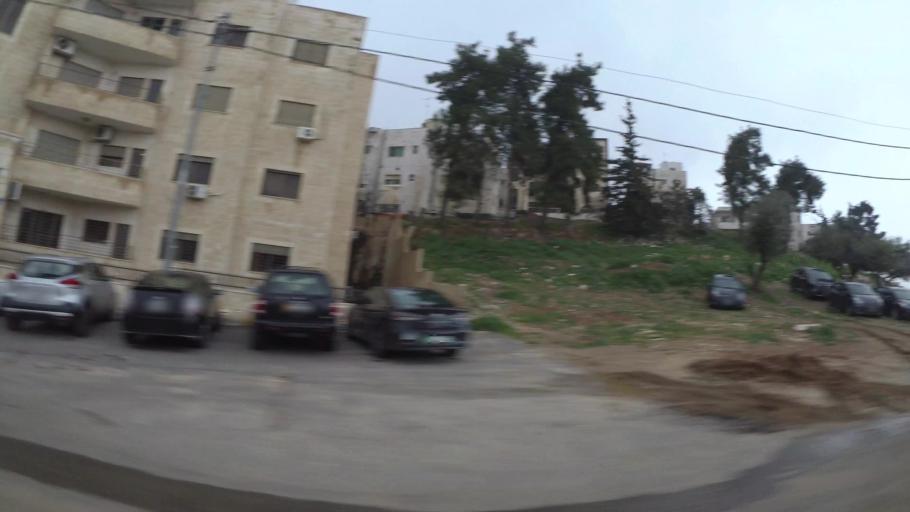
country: JO
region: Amman
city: Al Jubayhah
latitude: 31.9682
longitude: 35.8848
